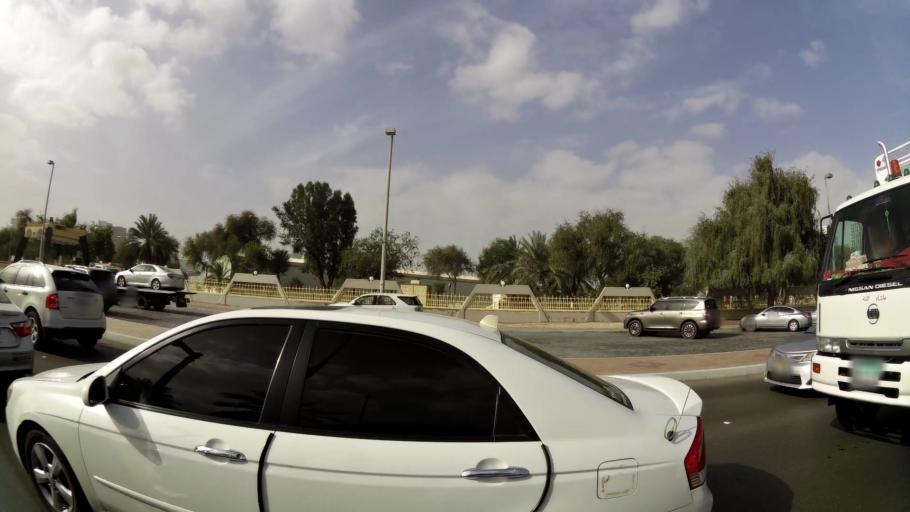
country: AE
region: Abu Dhabi
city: Abu Dhabi
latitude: 24.4296
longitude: 54.4424
